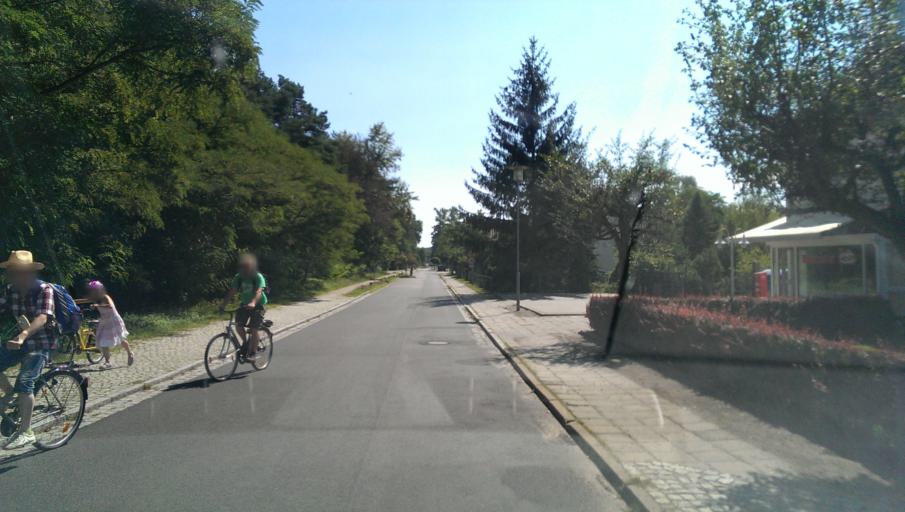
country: DE
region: Brandenburg
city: Michendorf
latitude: 52.2912
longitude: 13.0642
